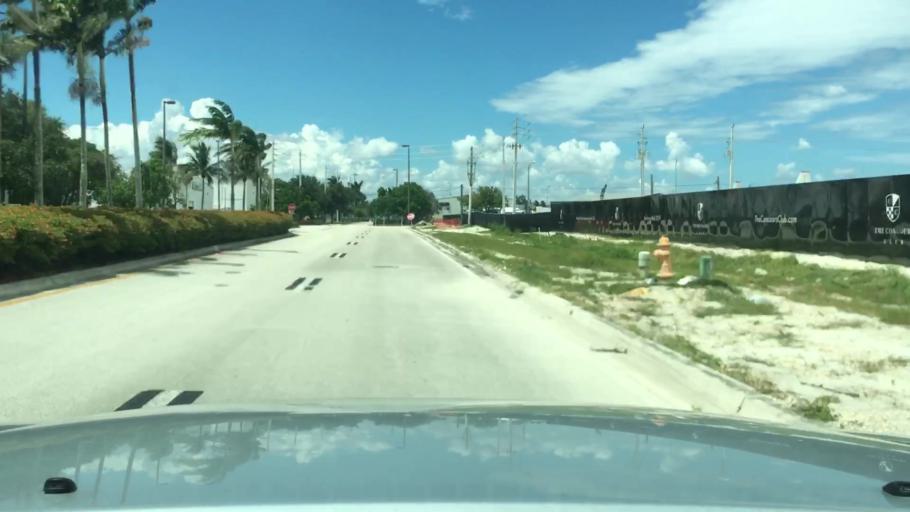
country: US
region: Florida
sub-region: Miami-Dade County
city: Opa-locka
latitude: 25.9049
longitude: -80.2678
